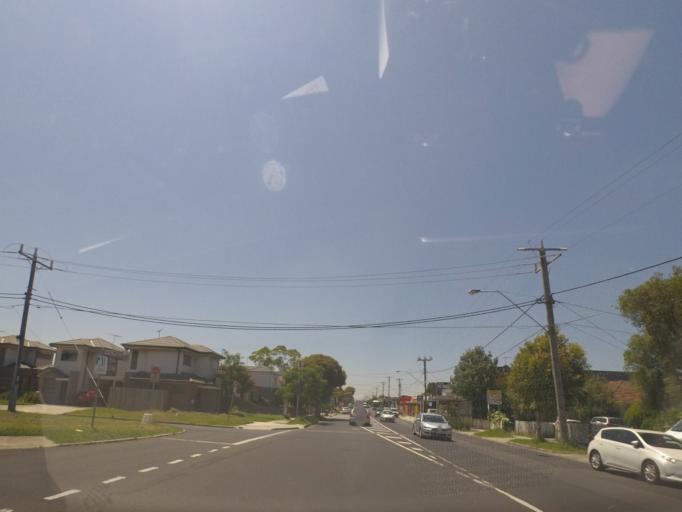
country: AU
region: Victoria
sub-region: Moreland
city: Pascoe Vale
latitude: -37.7328
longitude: 144.9381
